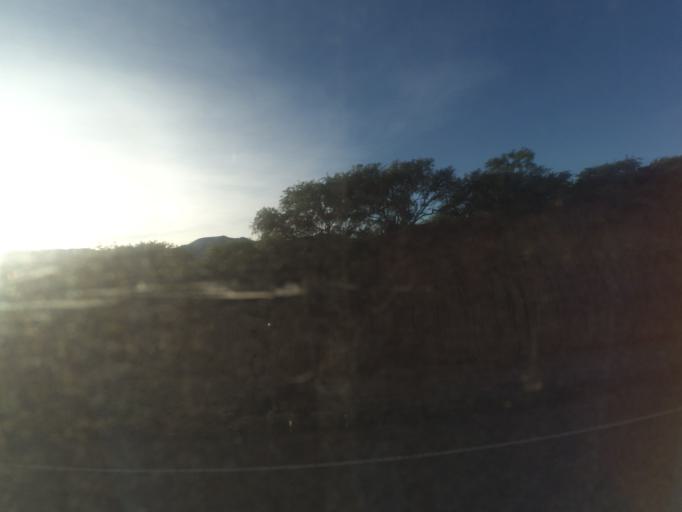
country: BO
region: Tarija
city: Tarija
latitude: -21.5220
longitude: -64.5664
